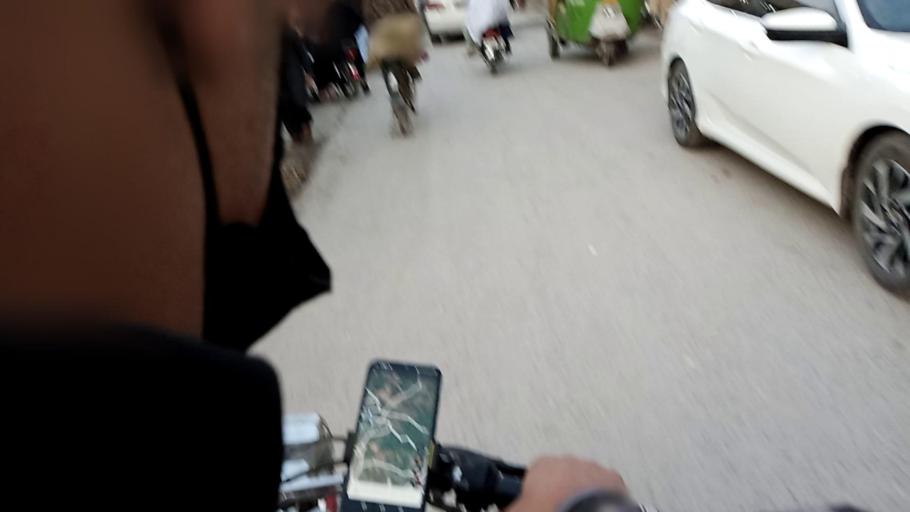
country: PK
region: Khyber Pakhtunkhwa
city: Peshawar
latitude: 34.0233
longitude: 71.4854
